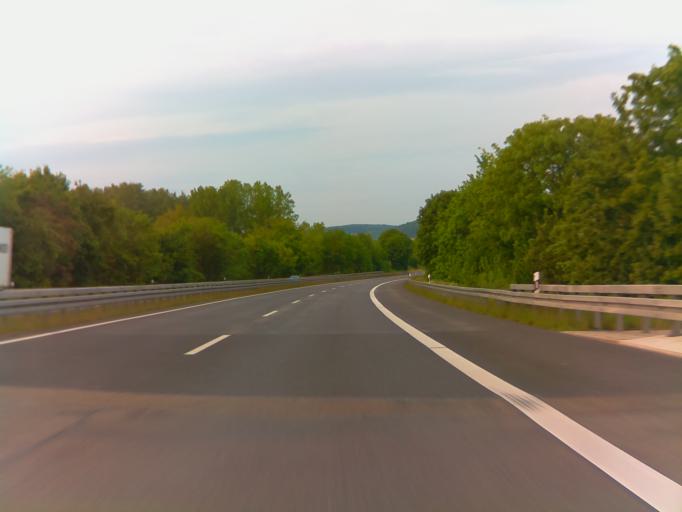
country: DE
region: Hesse
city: Fritzlar
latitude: 51.1585
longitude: 9.3018
